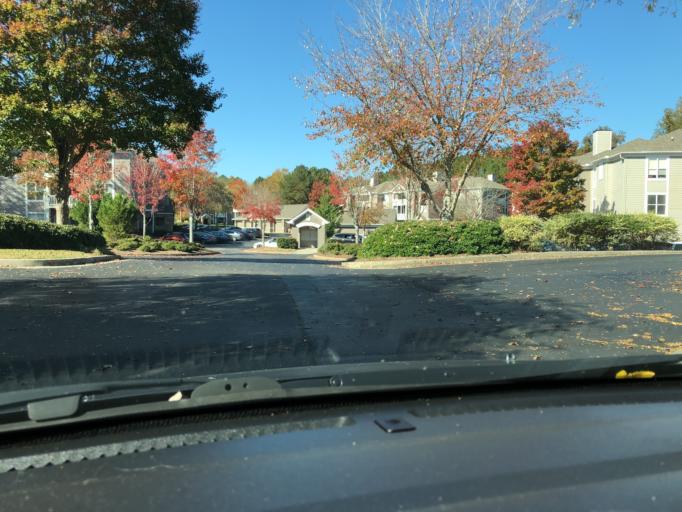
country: US
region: Georgia
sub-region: Fulton County
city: Johns Creek
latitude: 34.0168
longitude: -84.1800
